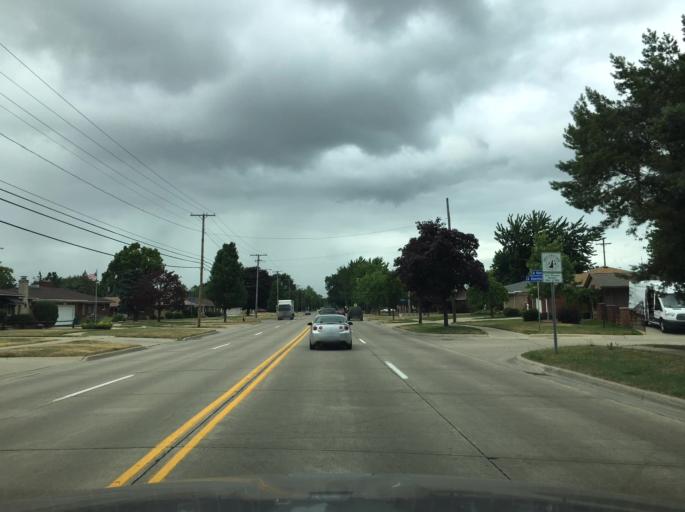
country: US
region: Michigan
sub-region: Macomb County
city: Saint Clair Shores
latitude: 42.4883
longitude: -82.8892
